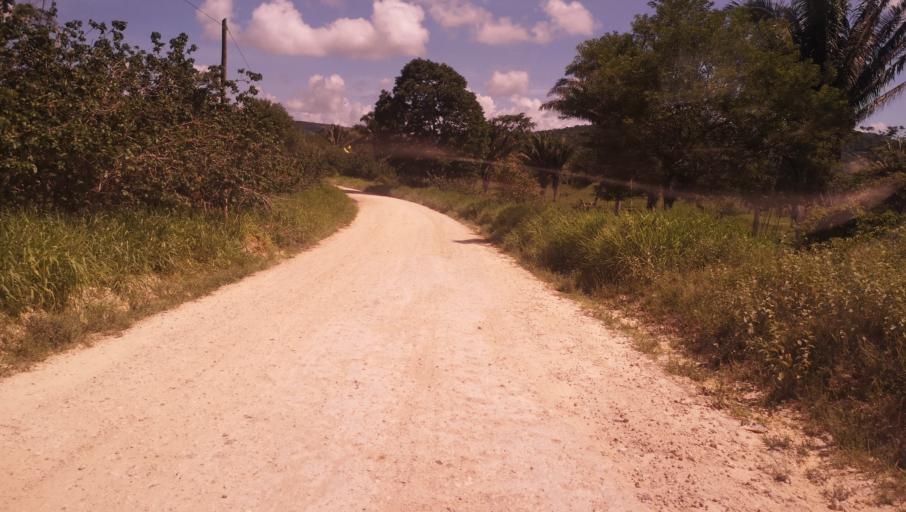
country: GT
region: Peten
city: Melchor de Mencos
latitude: 17.0151
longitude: -89.2432
